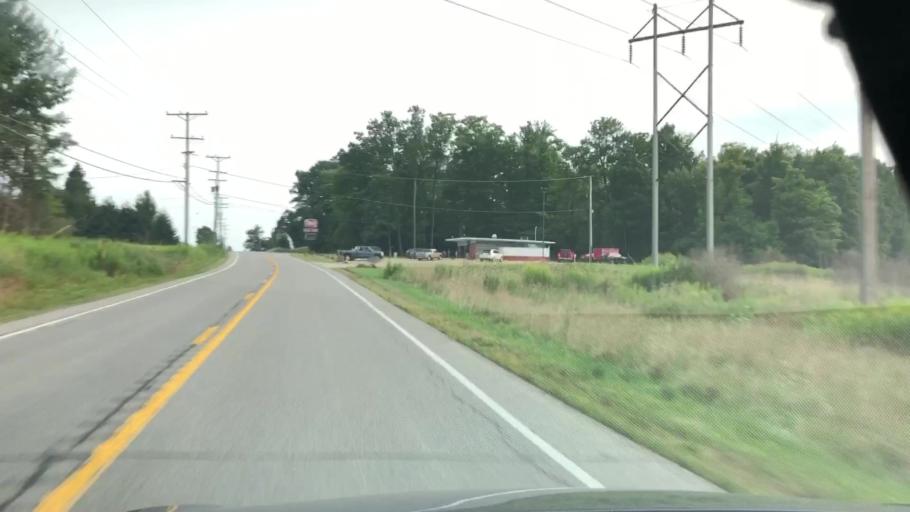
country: US
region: Pennsylvania
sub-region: Crawford County
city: Titusville
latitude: 41.5899
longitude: -79.6845
